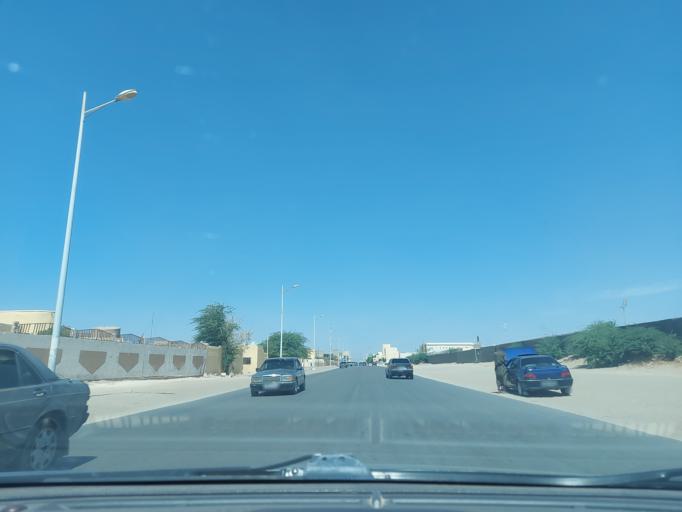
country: MR
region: Nouakchott
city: Nouakchott
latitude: 18.0803
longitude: -15.9699
